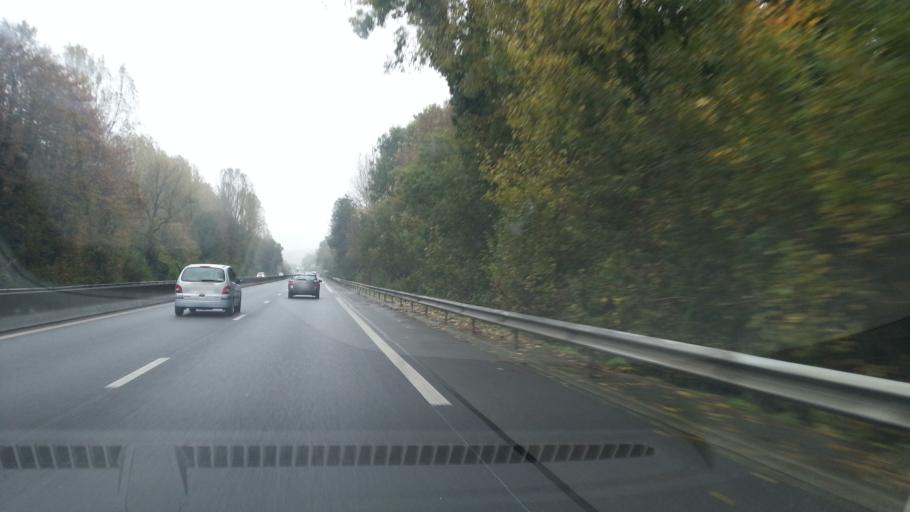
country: FR
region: Picardie
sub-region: Departement de l'Oise
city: Laigneville
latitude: 49.3052
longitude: 2.4530
